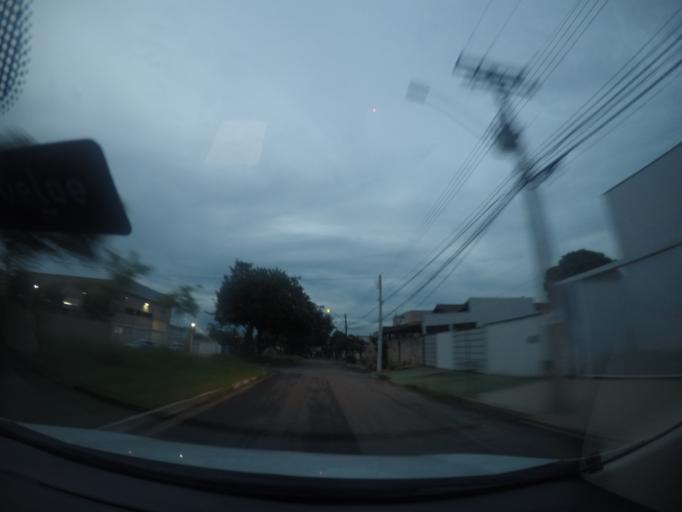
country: BR
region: Goias
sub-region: Goiania
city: Goiania
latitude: -16.6378
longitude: -49.2431
